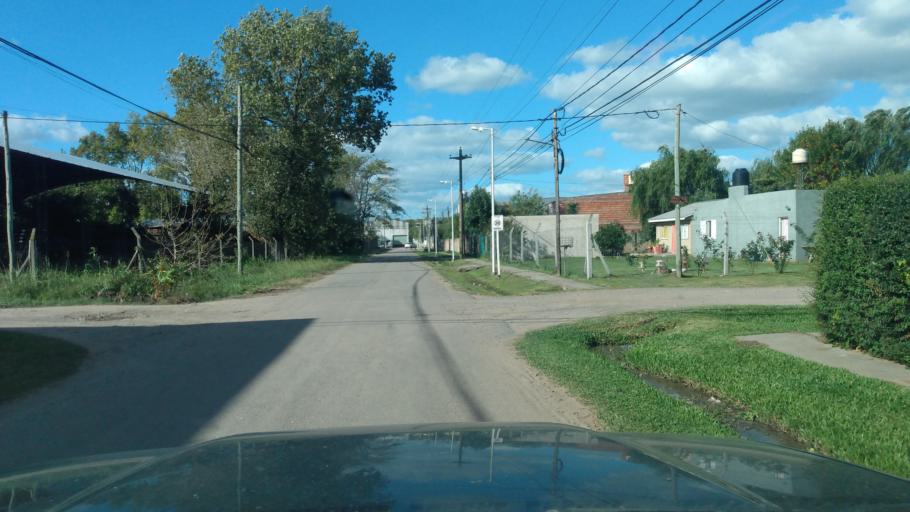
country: AR
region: Buenos Aires
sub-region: Partido de Lujan
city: Lujan
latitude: -34.5821
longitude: -59.0930
